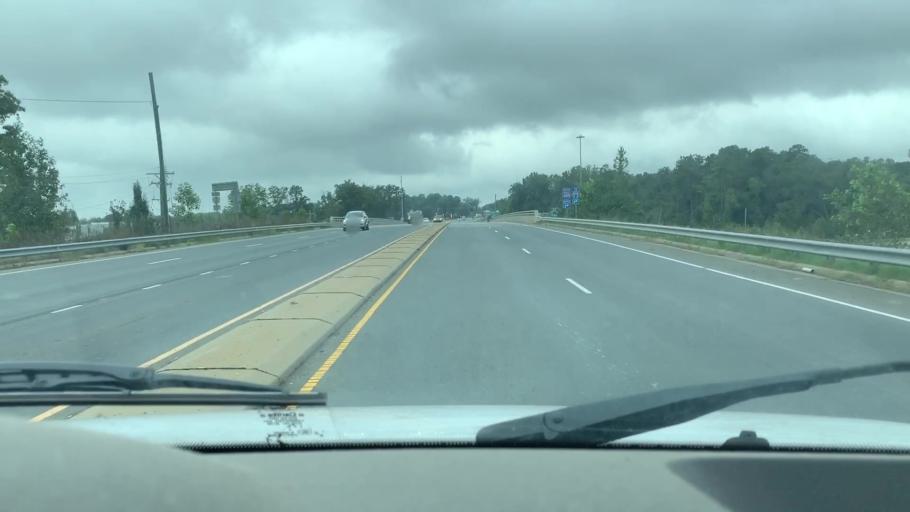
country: US
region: North Carolina
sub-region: Mecklenburg County
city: Huntersville
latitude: 35.3645
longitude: -80.8264
